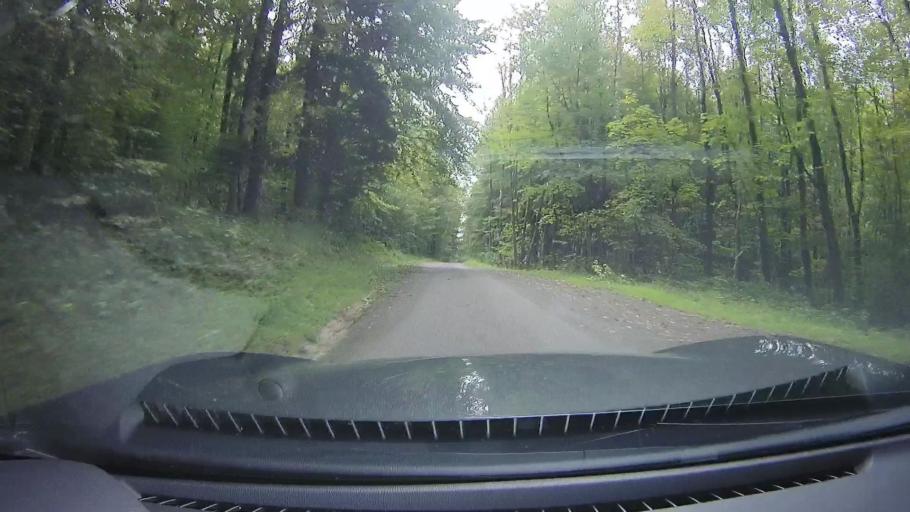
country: DE
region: Baden-Wuerttemberg
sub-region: Regierungsbezirk Stuttgart
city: Wustenrot
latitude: 49.0610
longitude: 9.4738
